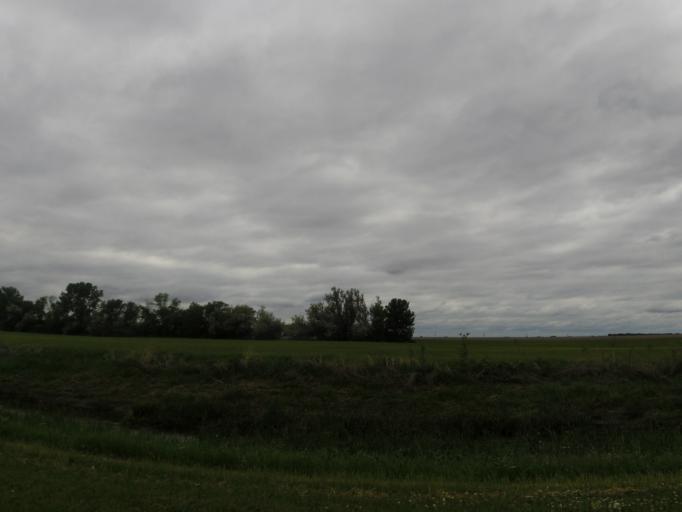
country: US
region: North Dakota
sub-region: Walsh County
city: Grafton
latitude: 48.6197
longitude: -97.4549
